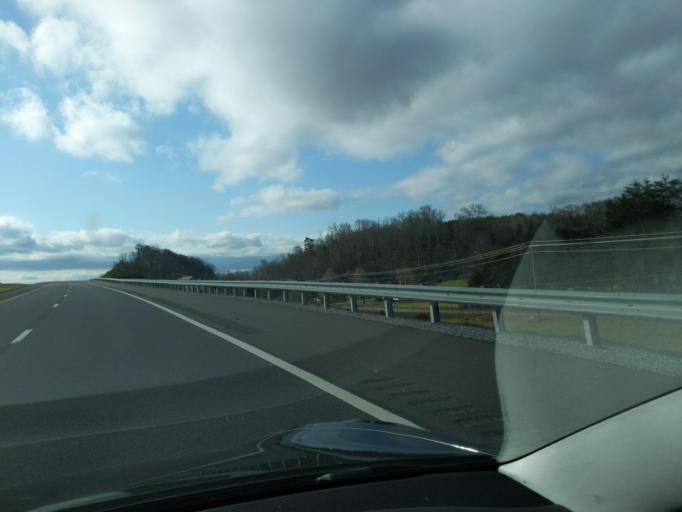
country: US
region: Tennessee
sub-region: Jefferson County
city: White Pine
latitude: 36.1396
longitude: -83.3423
